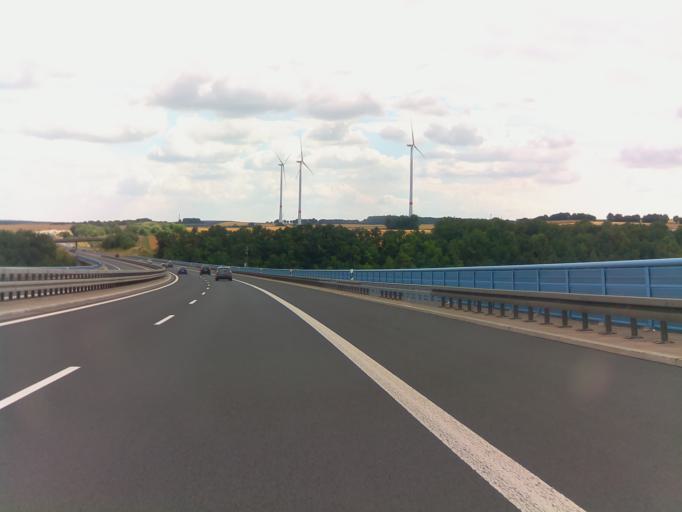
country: DE
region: Bavaria
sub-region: Regierungsbezirk Unterfranken
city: Munnerstadt
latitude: 50.2508
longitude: 10.2145
